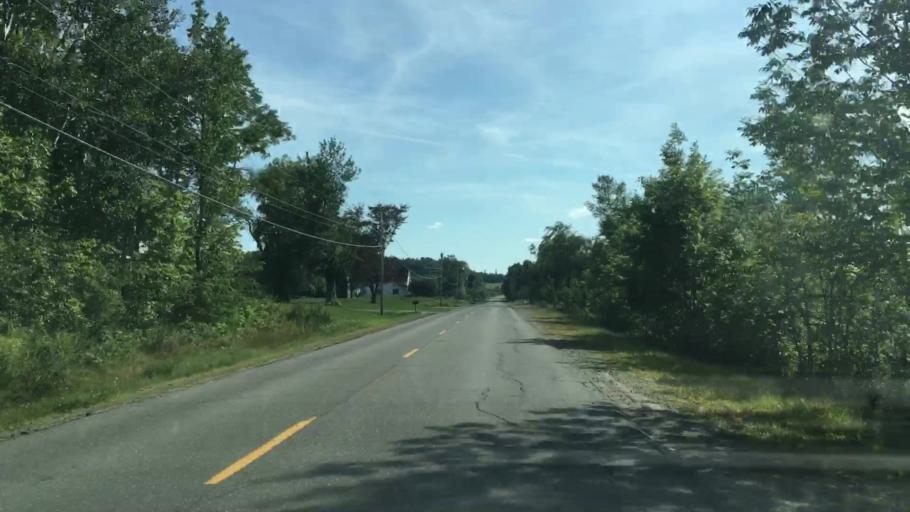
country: US
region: Maine
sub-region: Penobscot County
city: Lincoln
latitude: 45.3269
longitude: -68.5318
